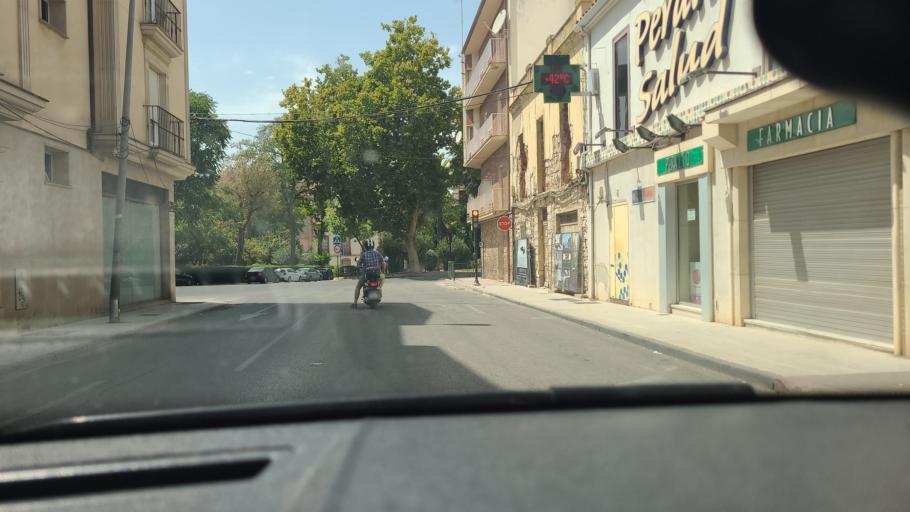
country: ES
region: Andalusia
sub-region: Provincia de Jaen
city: Linares
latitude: 38.0948
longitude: -3.6283
